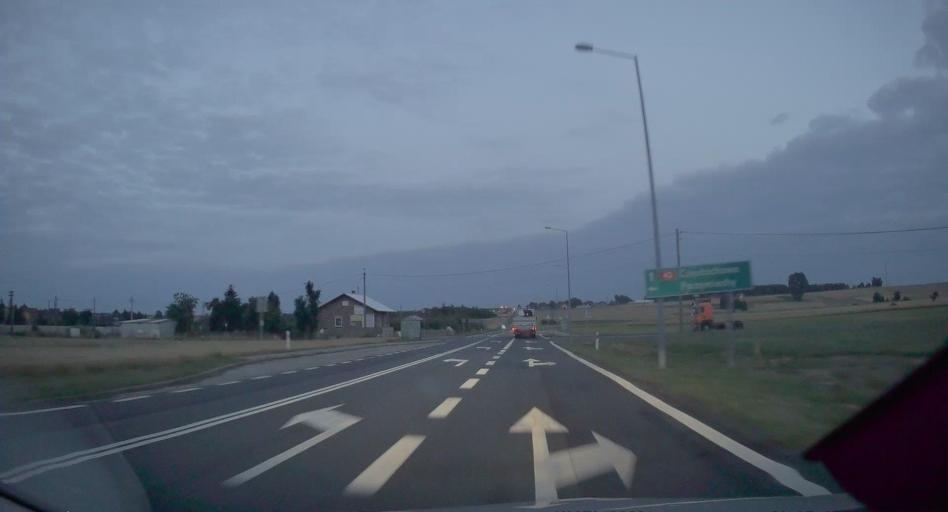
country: PL
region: Silesian Voivodeship
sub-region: Powiat klobucki
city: Opatow
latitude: 50.9346
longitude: 18.8515
